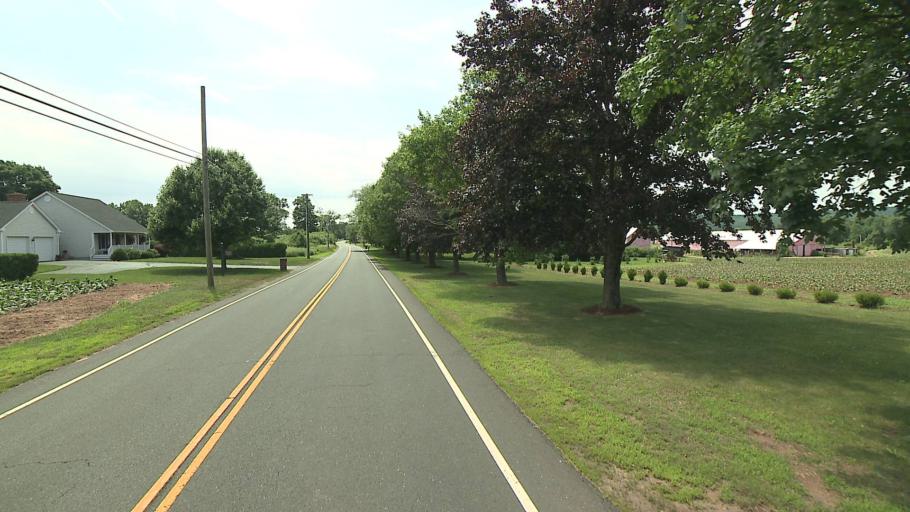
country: US
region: Connecticut
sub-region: Hartford County
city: Suffield Depot
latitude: 41.9779
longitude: -72.6954
